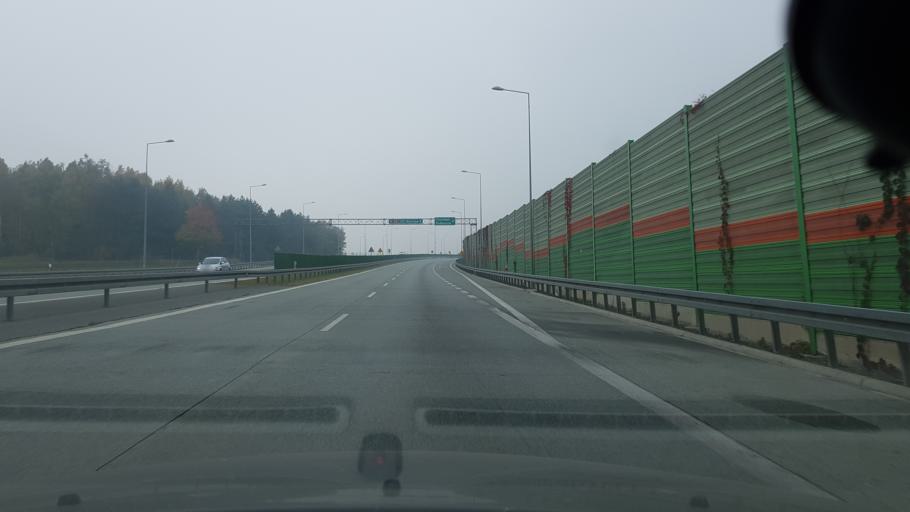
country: PL
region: Lodz Voivodeship
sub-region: Powiat rawski
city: Rawa Mazowiecka
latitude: 51.7078
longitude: 20.2196
